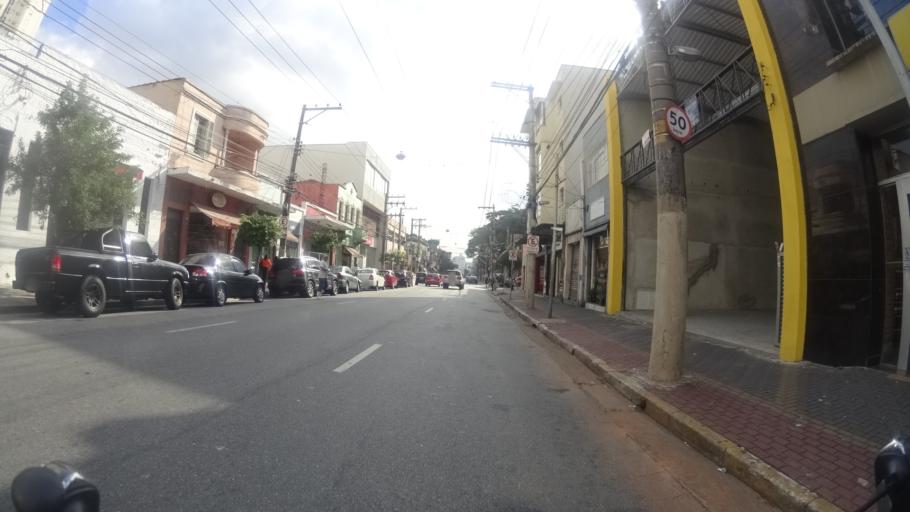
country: BR
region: Sao Paulo
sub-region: Sao Paulo
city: Sao Paulo
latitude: -23.5551
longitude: -46.6053
